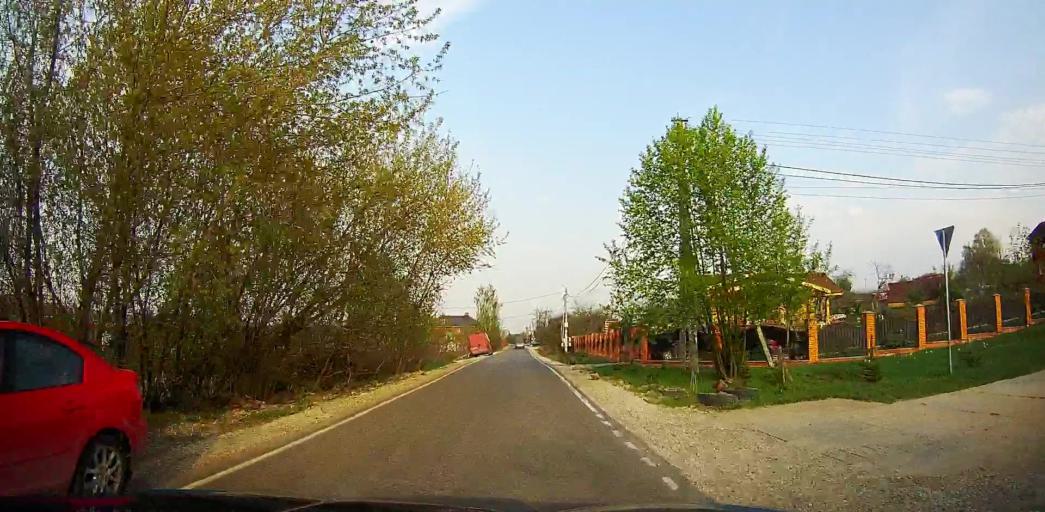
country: RU
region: Moskovskaya
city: Andreyevskoye
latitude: 55.5581
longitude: 37.9137
